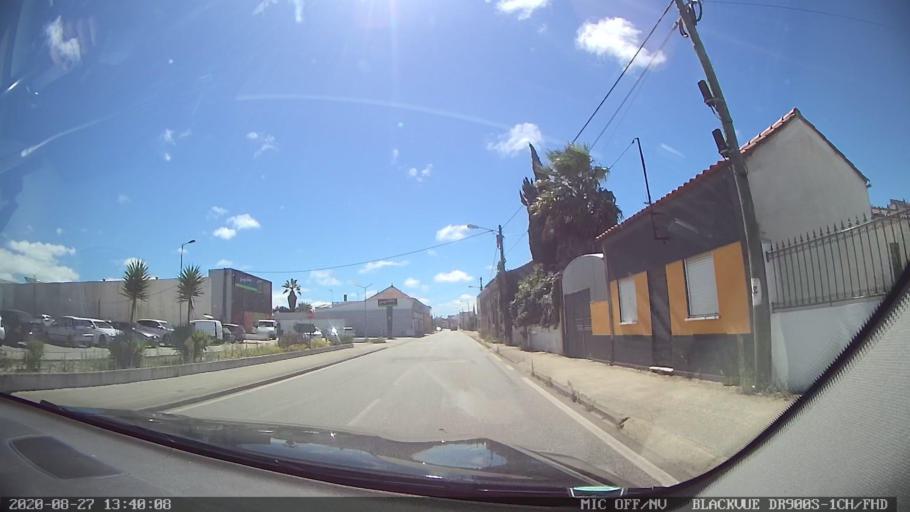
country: PT
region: Coimbra
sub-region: Mira
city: Mira
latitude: 40.4361
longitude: -8.7285
